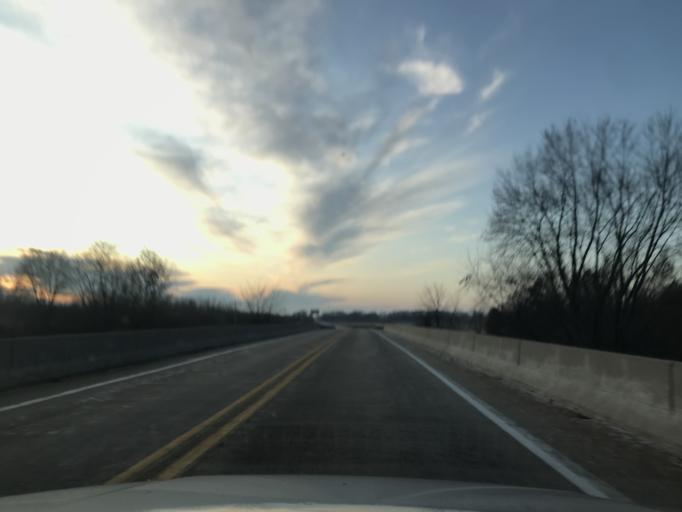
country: US
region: Illinois
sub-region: Henderson County
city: Oquawka
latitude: 41.0190
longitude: -90.8092
